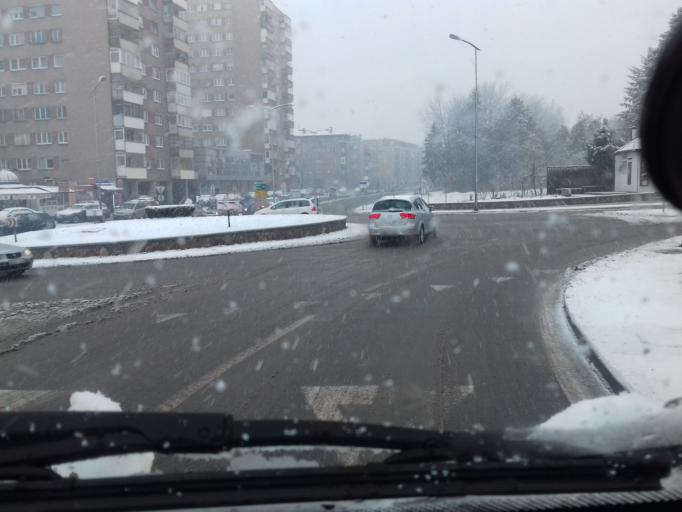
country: BA
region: Federation of Bosnia and Herzegovina
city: Zenica
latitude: 44.1961
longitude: 17.9109
